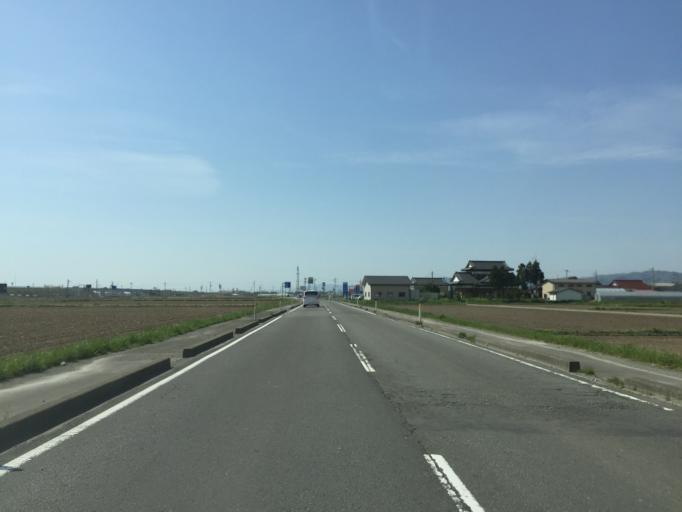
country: JP
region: Miyagi
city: Watari
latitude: 38.0407
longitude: 140.8900
